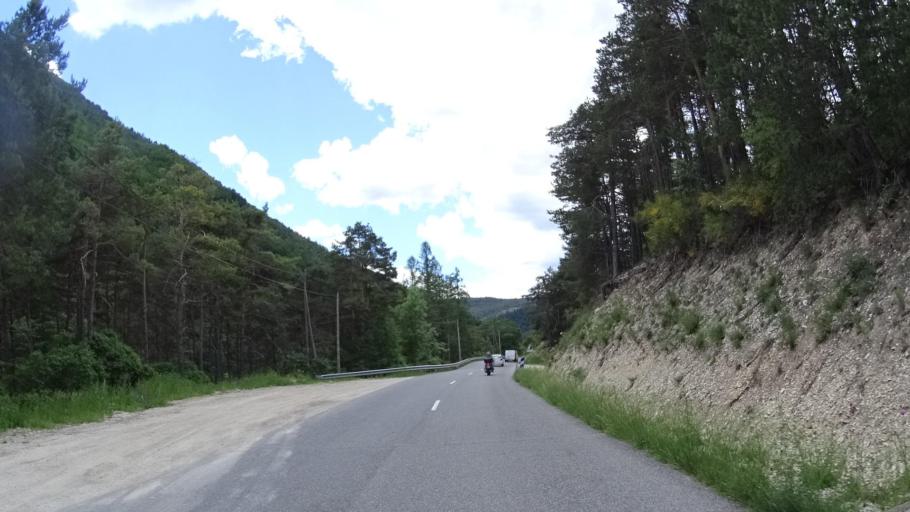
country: FR
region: Provence-Alpes-Cote d'Azur
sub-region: Departement des Alpes-de-Haute-Provence
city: Annot
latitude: 44.0339
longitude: 6.5600
